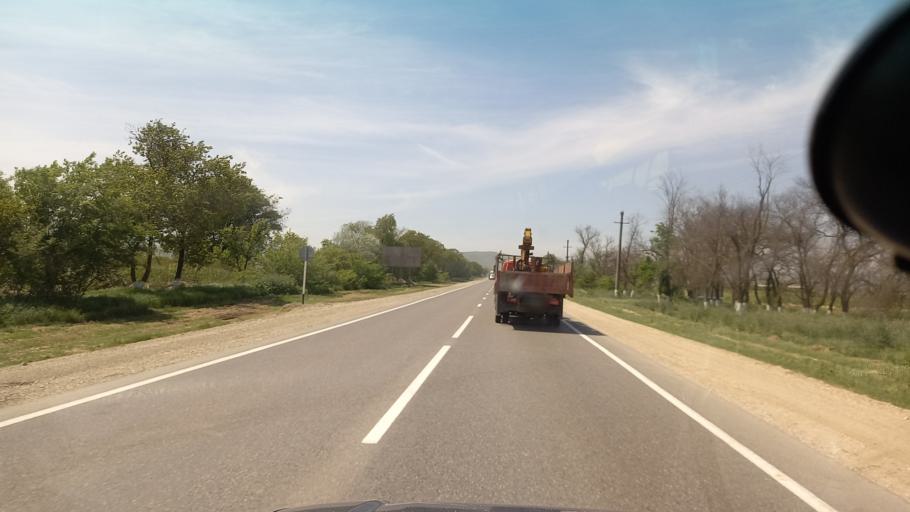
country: RU
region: Dagestan
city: Manas
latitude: 42.7083
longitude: 47.6854
